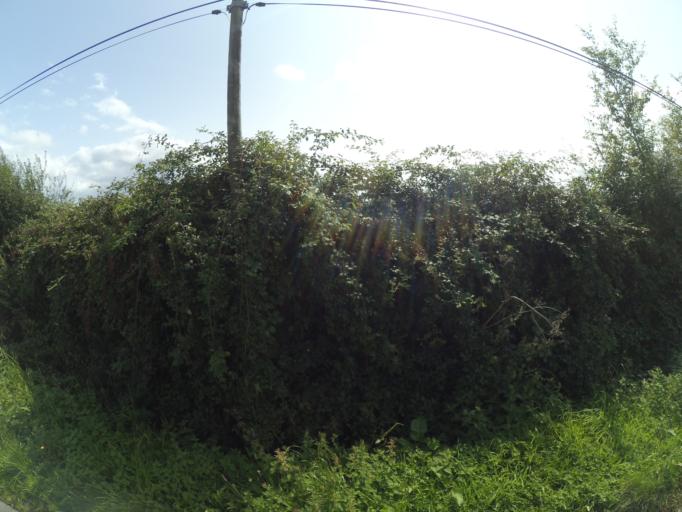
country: FR
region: Pays de la Loire
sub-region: Departement de la Vendee
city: La Bruffiere
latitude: 47.0255
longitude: -1.2311
